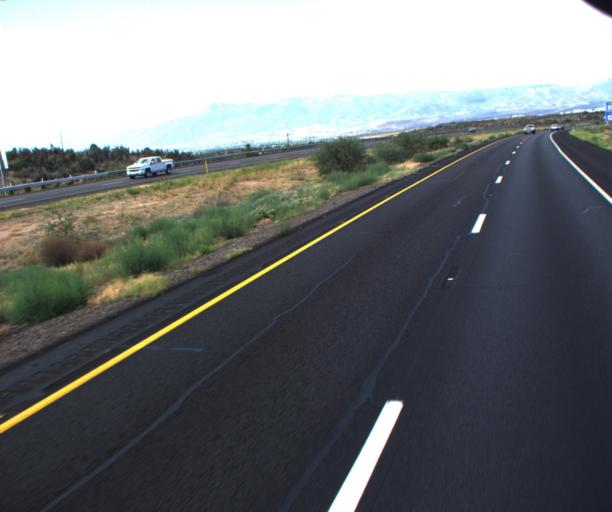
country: US
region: Arizona
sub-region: Yavapai County
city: Camp Verde
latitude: 34.6179
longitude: -111.8469
